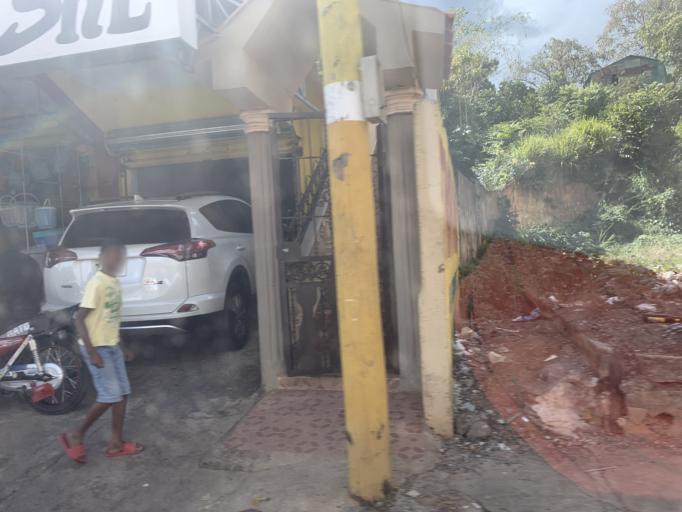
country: DO
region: Monte Plata
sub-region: Yamasa
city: Yamasa
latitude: 18.7712
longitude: -70.0254
